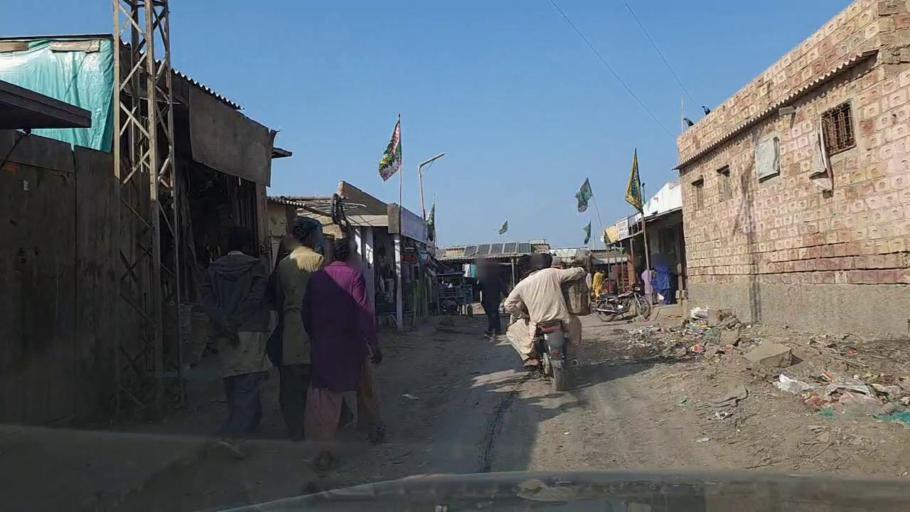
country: PK
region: Sindh
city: Keti Bandar
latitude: 24.1438
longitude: 67.4507
